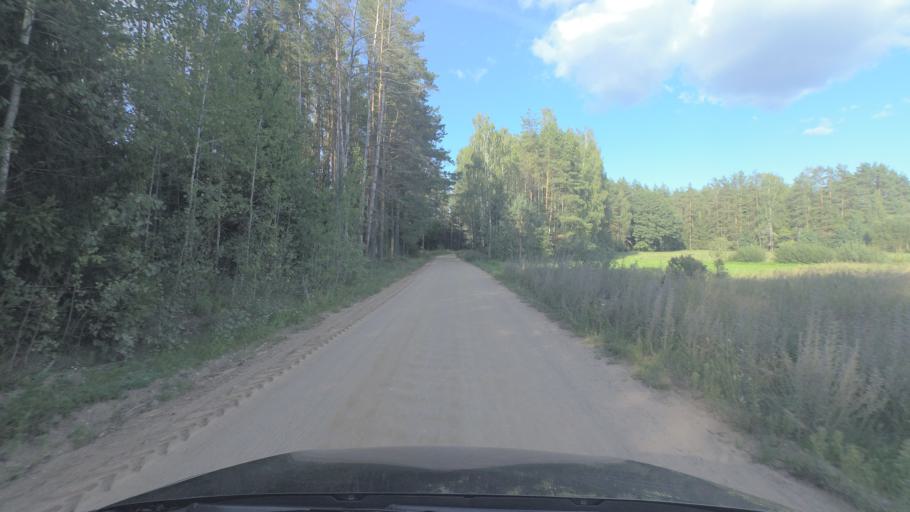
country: LT
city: Pabrade
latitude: 55.1476
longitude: 25.7487
